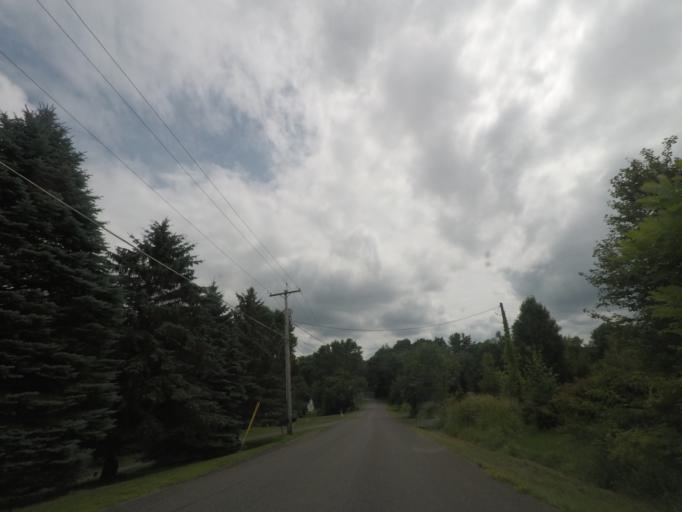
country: US
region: New York
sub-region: Saratoga County
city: Stillwater
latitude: 43.0041
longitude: -73.6866
